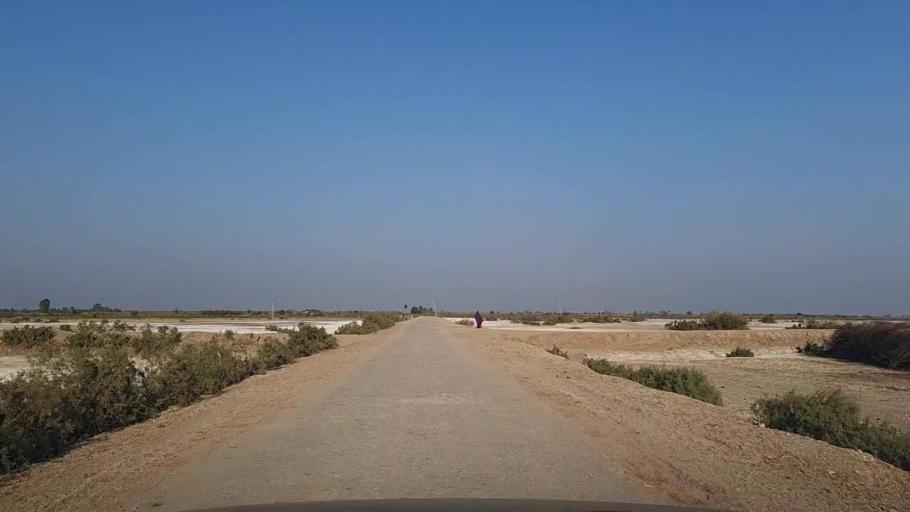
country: PK
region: Sindh
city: Tando Mittha Khan
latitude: 25.9296
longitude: 69.0650
